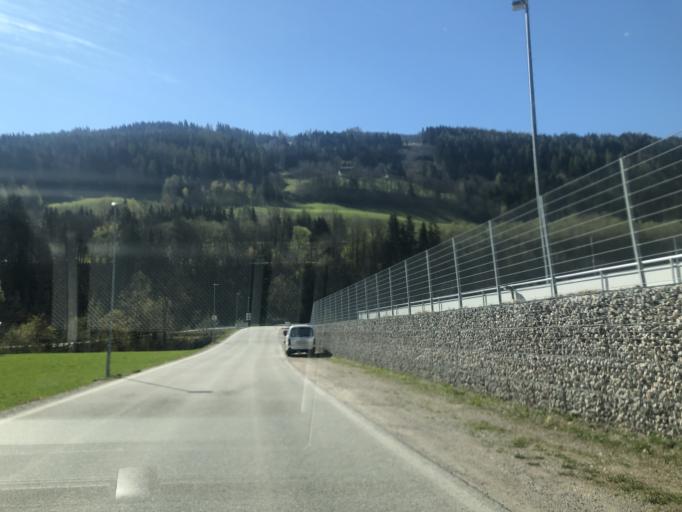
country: AT
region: Styria
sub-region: Politischer Bezirk Liezen
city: Schladming
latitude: 47.4002
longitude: 13.7055
